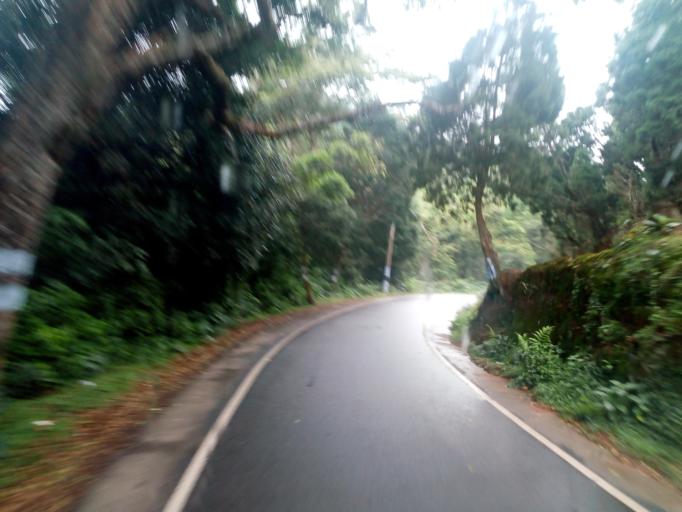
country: IN
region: Tamil Nadu
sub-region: Nilgiri
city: Wellington
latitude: 11.3619
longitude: 76.8372
